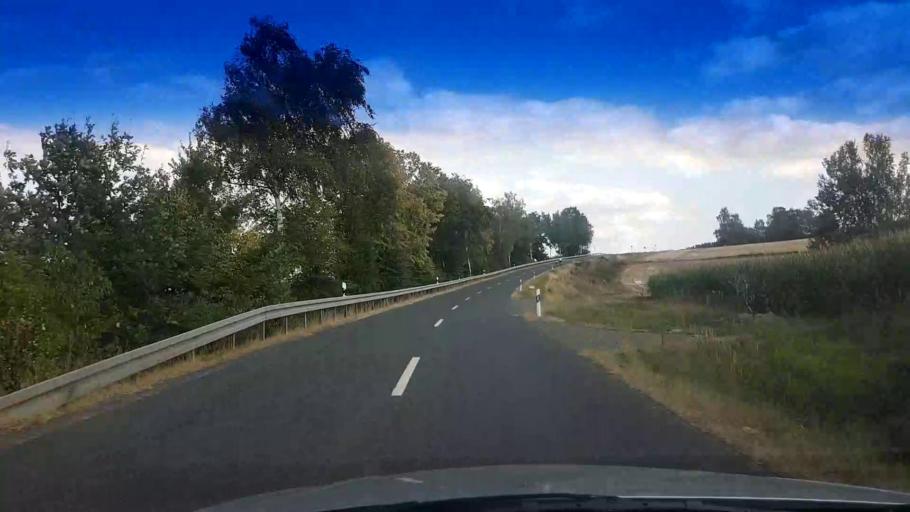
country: DE
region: Bavaria
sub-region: Upper Palatinate
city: Waldsassen
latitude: 50.0204
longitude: 12.3562
